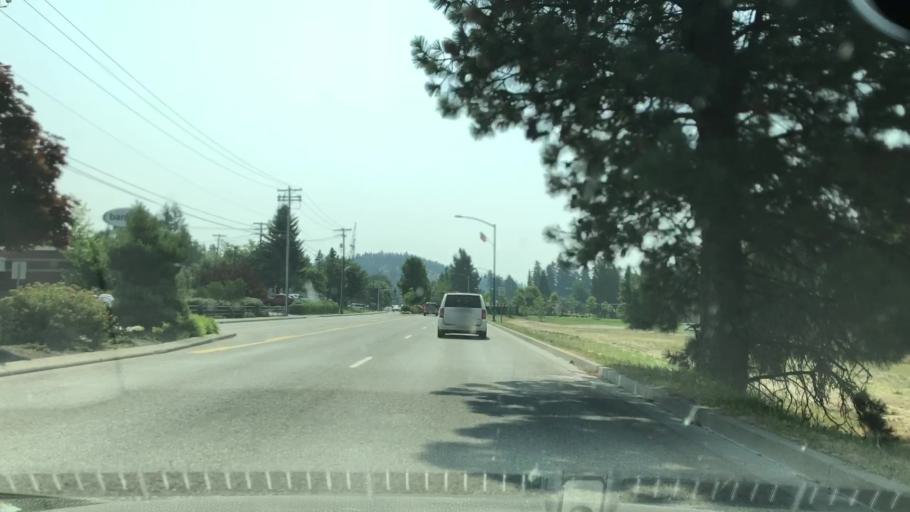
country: US
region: Idaho
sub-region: Kootenai County
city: Coeur d'Alene
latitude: 47.6818
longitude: -116.7932
